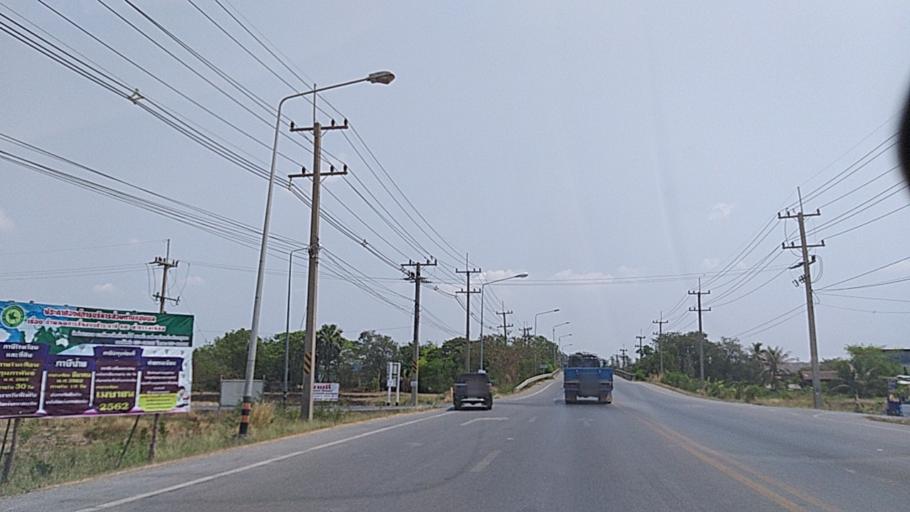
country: TH
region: Bangkok
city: Nong Chok
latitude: 13.9698
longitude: 100.9575
